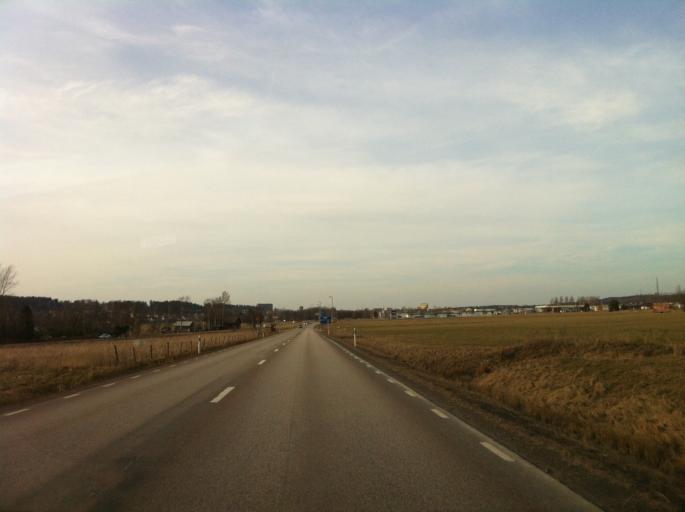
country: SE
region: Vaermland
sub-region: Kristinehamns Kommun
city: Kristinehamn
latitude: 59.2909
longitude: 14.1324
